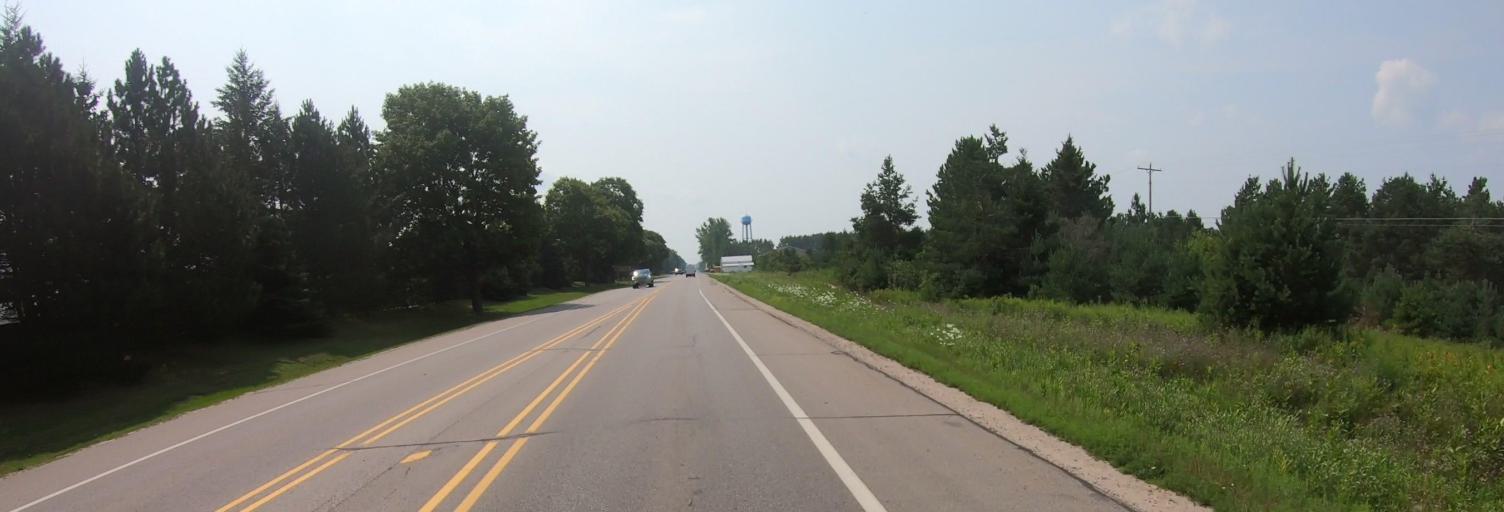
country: US
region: Michigan
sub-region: Luce County
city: Newberry
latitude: 46.3315
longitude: -85.5097
